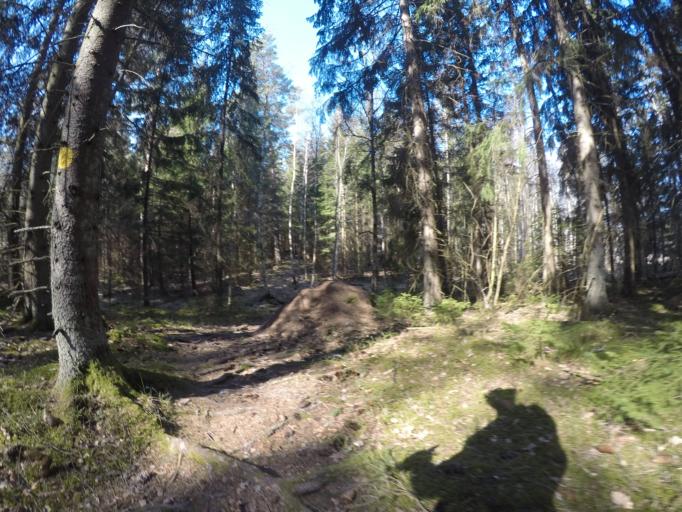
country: SE
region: Vaestmanland
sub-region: Hallstahammars Kommun
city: Kolback
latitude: 59.5364
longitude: 16.2806
